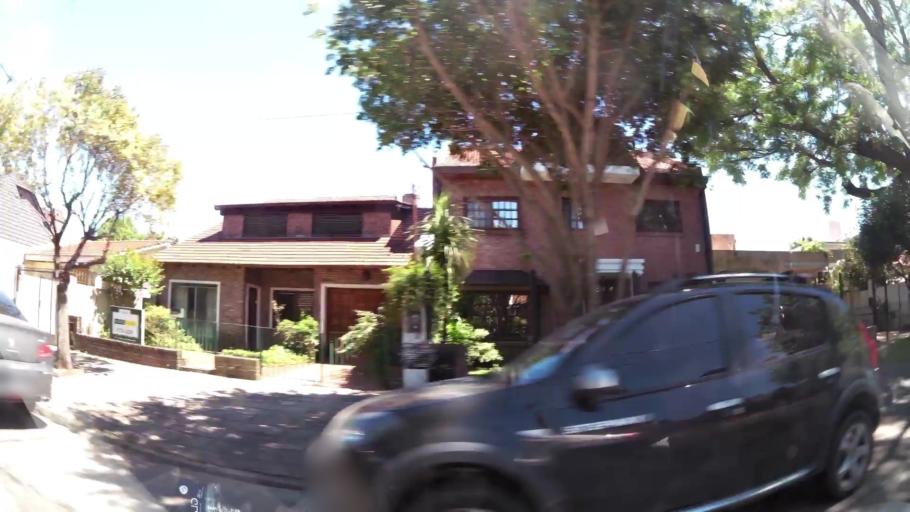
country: AR
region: Buenos Aires
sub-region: Partido de San Isidro
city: San Isidro
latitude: -34.4728
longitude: -58.5258
